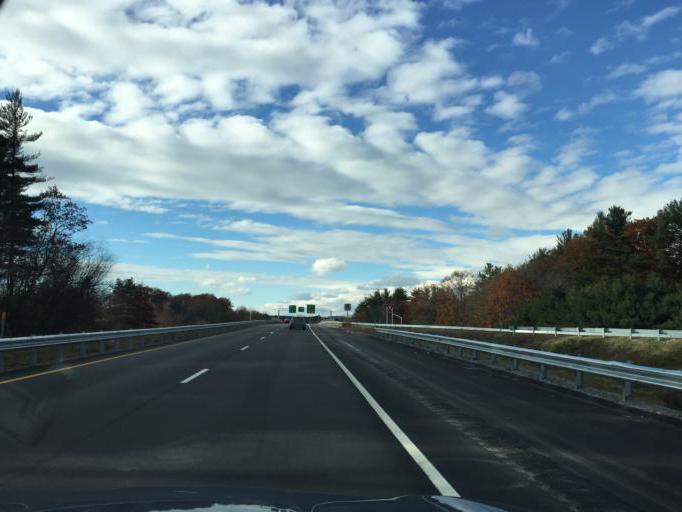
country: US
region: New Hampshire
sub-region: Hillsborough County
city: Bedford
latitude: 42.9483
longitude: -71.4704
